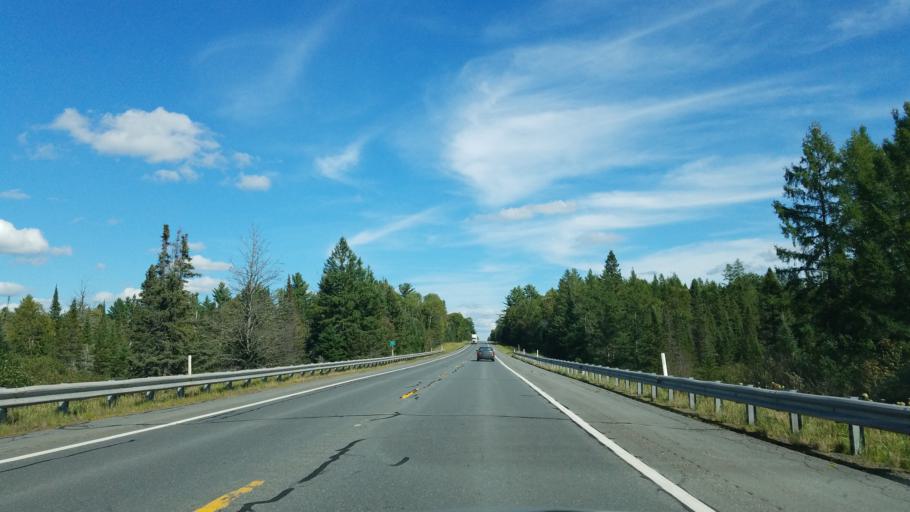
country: US
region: Michigan
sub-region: Baraga County
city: L'Anse
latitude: 46.5788
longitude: -88.4139
